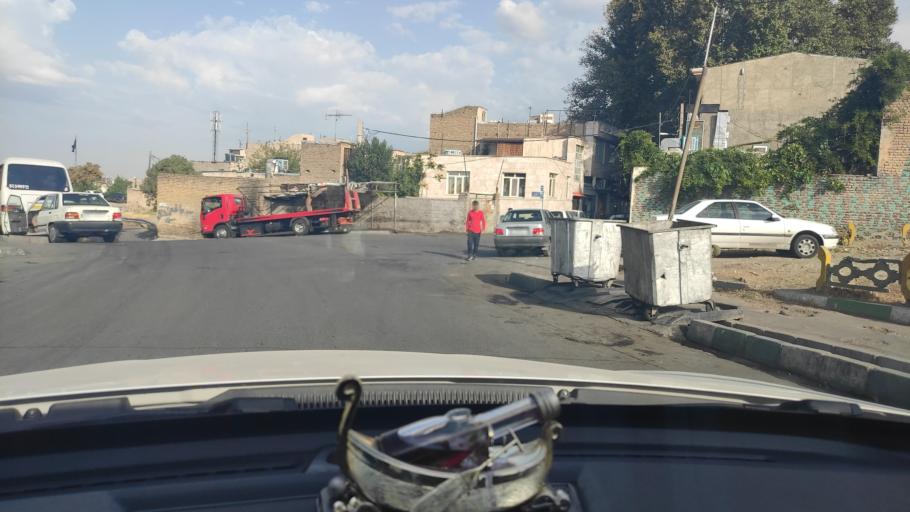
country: IR
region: Tehran
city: Tehran
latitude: 35.7544
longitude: 51.2786
